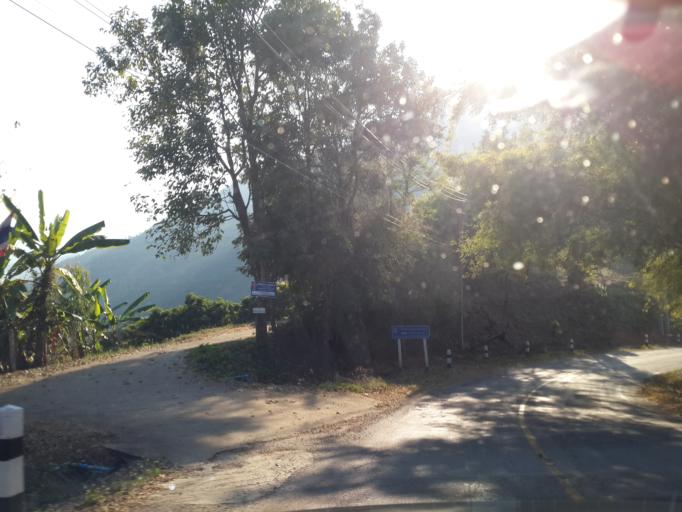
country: TH
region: Chiang Mai
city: Chai Prakan
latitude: 19.8268
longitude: 99.1015
